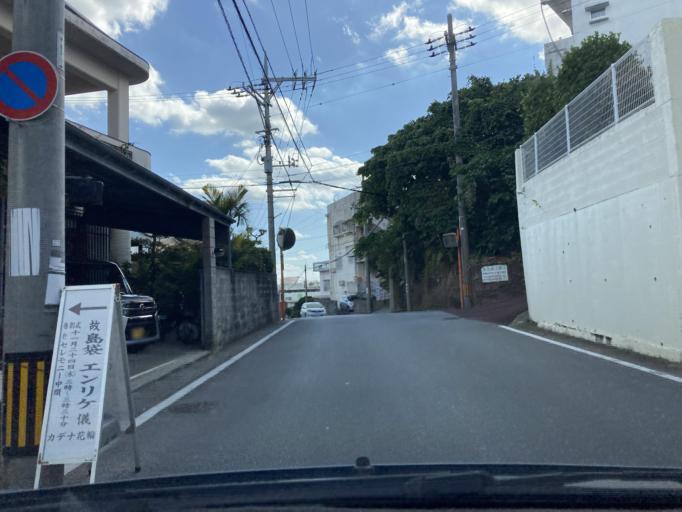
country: JP
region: Okinawa
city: Okinawa
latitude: 26.3426
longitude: 127.8058
